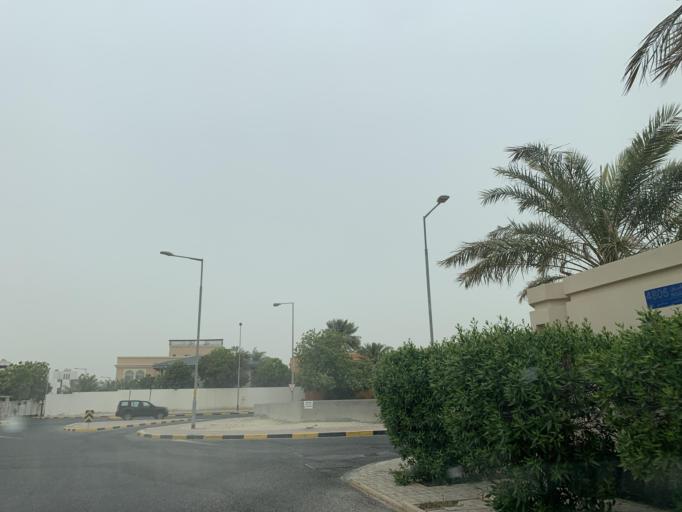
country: BH
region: Northern
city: Ar Rifa'
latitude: 26.1473
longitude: 50.5320
